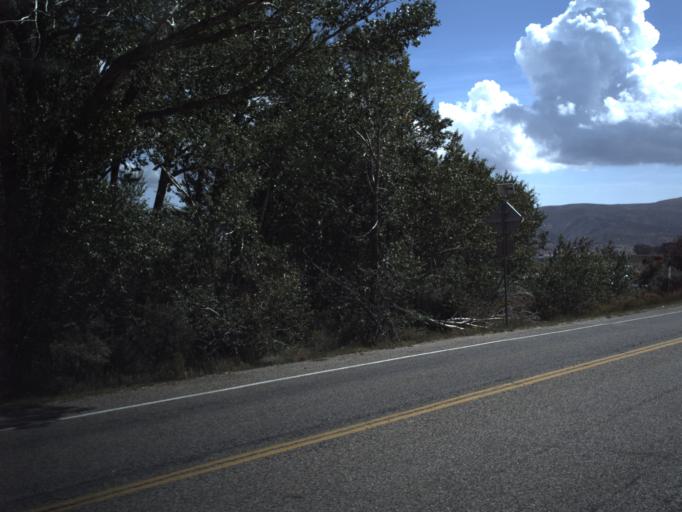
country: US
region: Utah
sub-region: Rich County
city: Randolph
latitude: 41.8469
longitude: -111.3520
